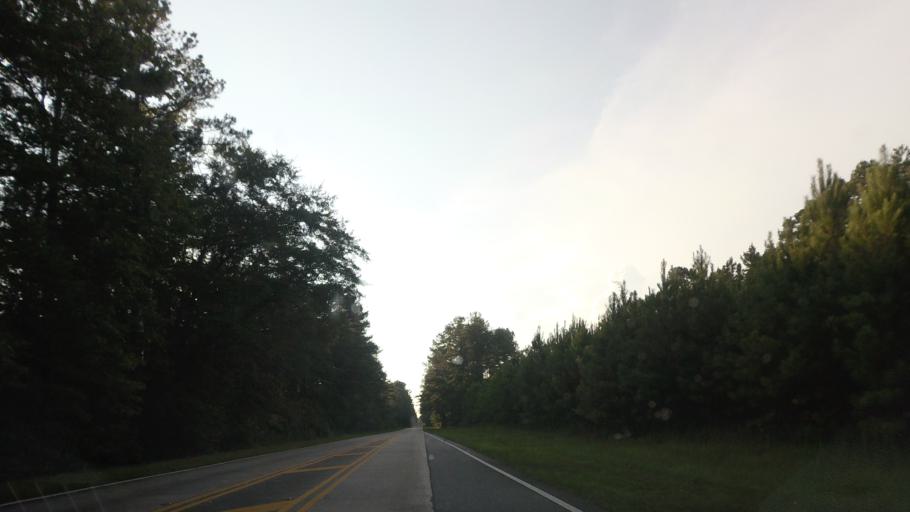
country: US
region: Georgia
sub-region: Bibb County
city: Macon
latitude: 32.9394
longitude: -83.7374
